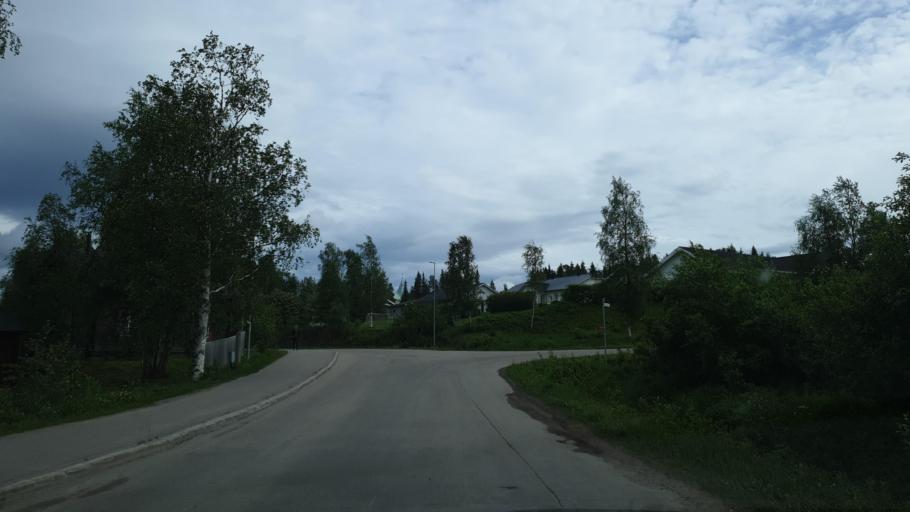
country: SE
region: Norrbotten
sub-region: Gallivare Kommun
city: Gaellivare
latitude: 67.1278
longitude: 20.6523
